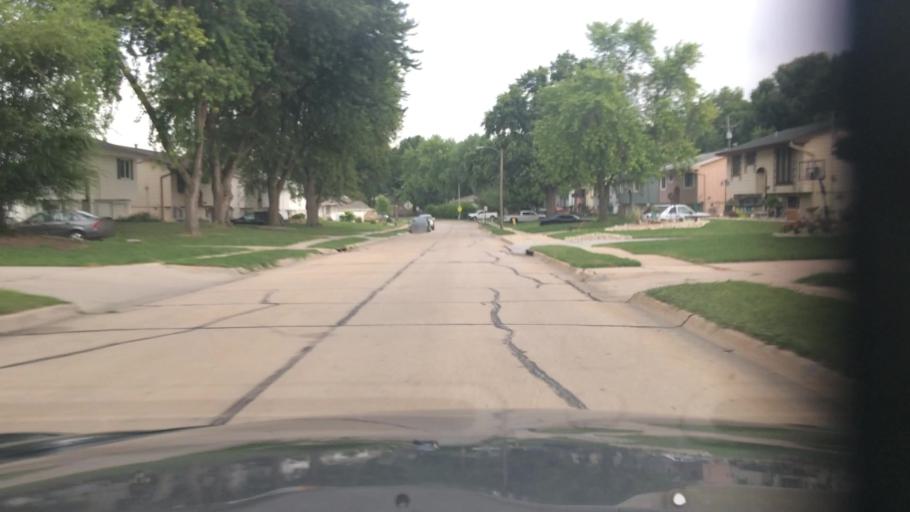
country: US
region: Nebraska
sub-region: Sarpy County
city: La Vista
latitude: 41.1859
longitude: -96.0519
